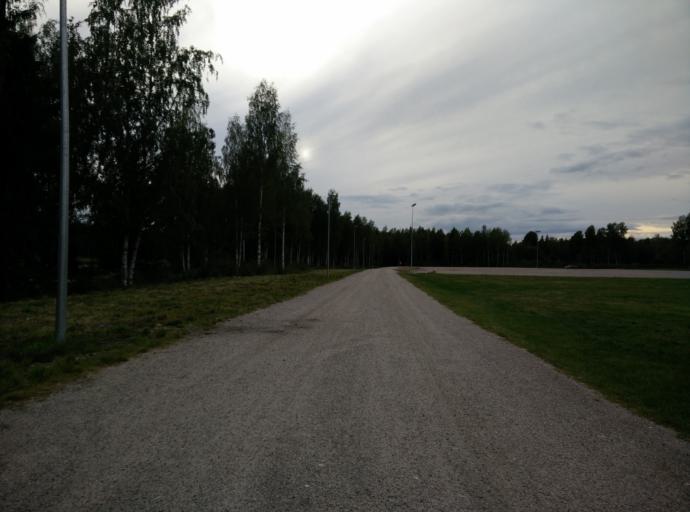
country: FI
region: Haeme
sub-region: Haemeenlinna
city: Haemeenlinna
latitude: 60.9845
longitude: 24.4844
